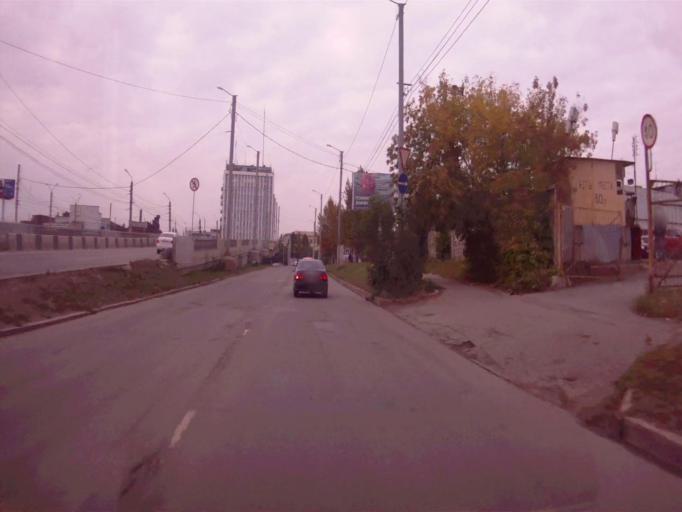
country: RU
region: Chelyabinsk
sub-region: Gorod Chelyabinsk
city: Chelyabinsk
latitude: 55.1392
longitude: 61.4110
